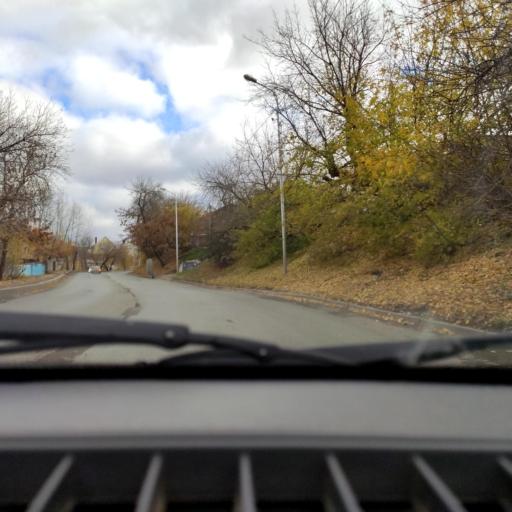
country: RU
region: Bashkortostan
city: Ufa
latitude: 54.7407
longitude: 55.9364
